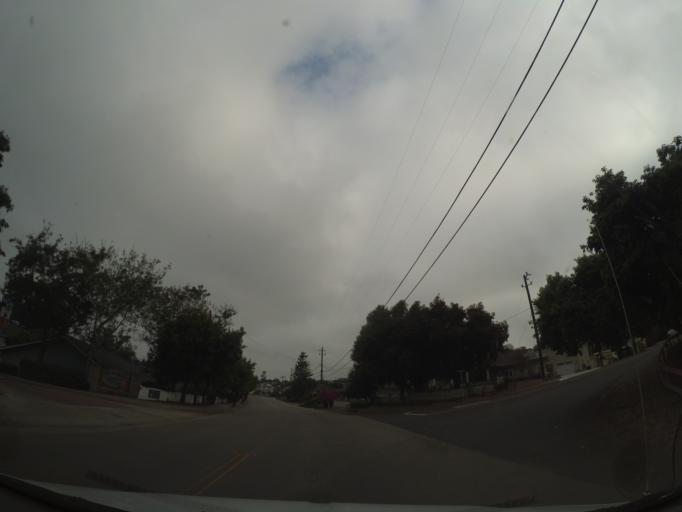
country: US
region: California
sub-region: San Luis Obispo County
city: Morro Bay
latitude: 35.3543
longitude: -120.8438
